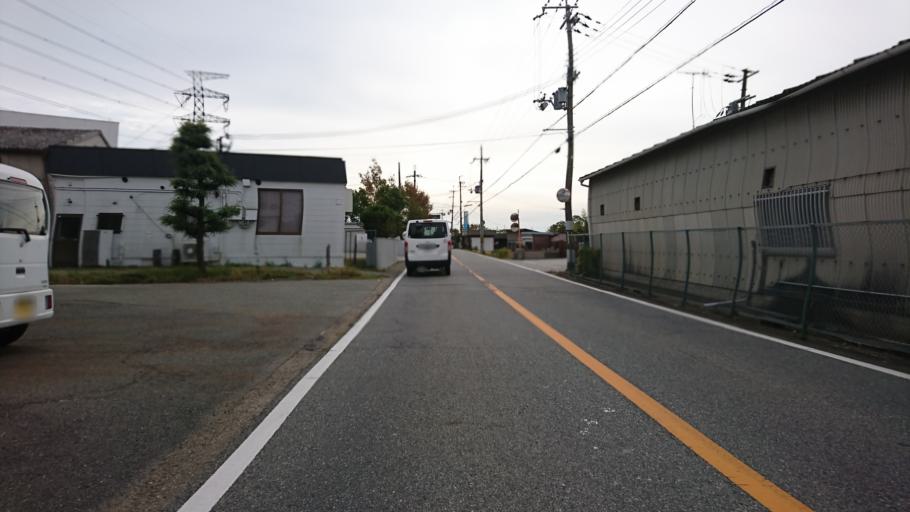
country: JP
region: Hyogo
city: Ono
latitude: 34.7996
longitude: 134.9247
